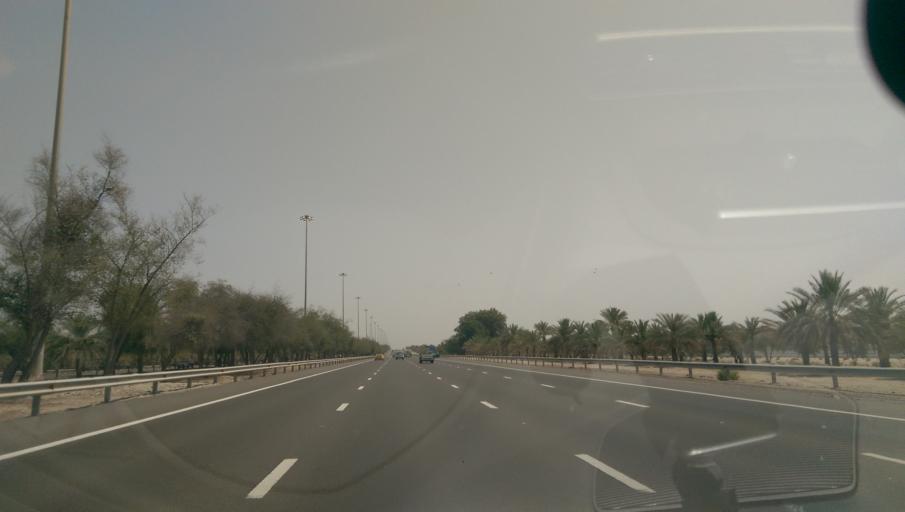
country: AE
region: Abu Dhabi
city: Abu Dhabi
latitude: 24.4896
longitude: 54.6771
